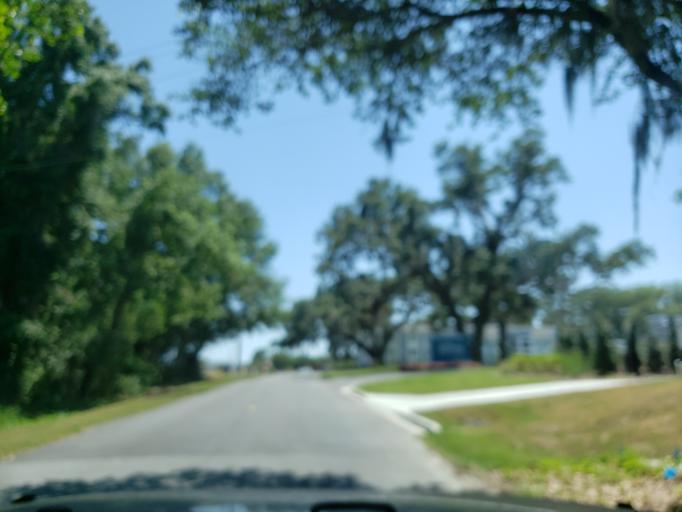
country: US
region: Georgia
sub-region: Chatham County
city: Thunderbolt
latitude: 32.0697
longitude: -81.0490
